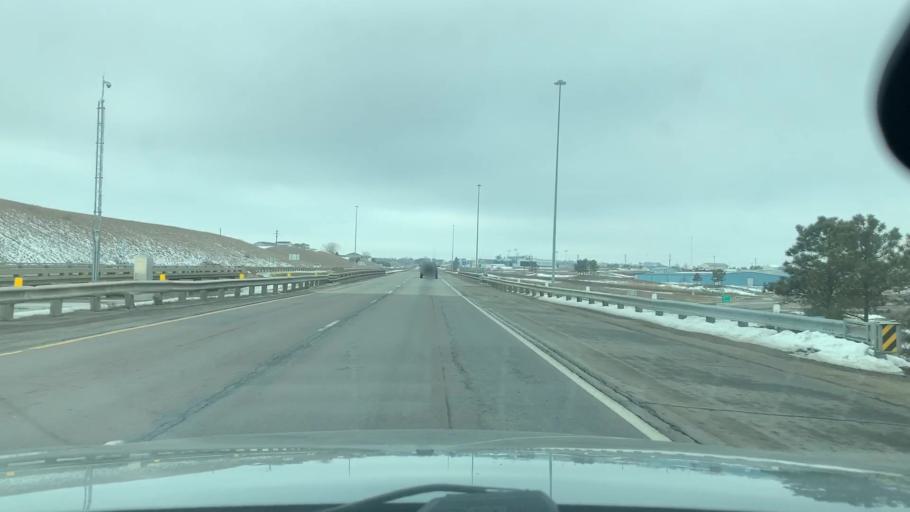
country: US
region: North Dakota
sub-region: Morton County
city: Mandan
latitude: 46.8378
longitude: -100.8733
